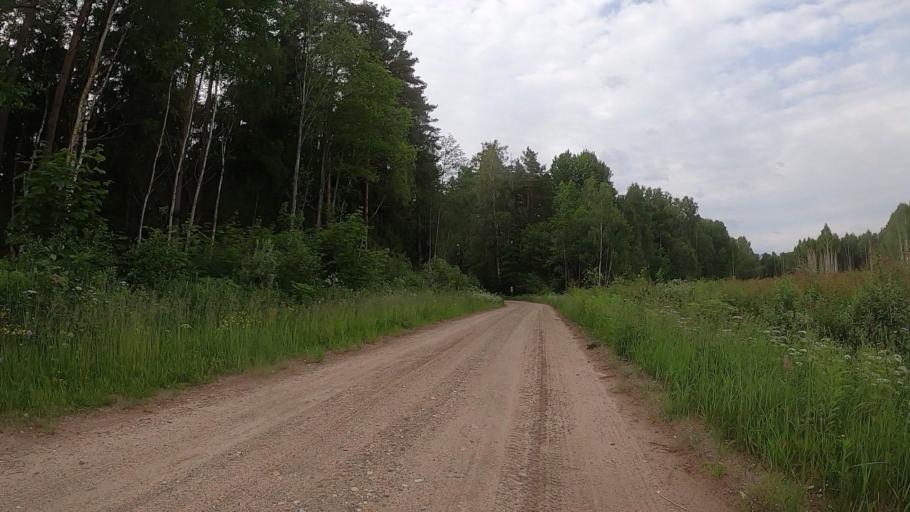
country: LV
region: Ozolnieku
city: Ozolnieki
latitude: 56.7240
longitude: 23.7906
